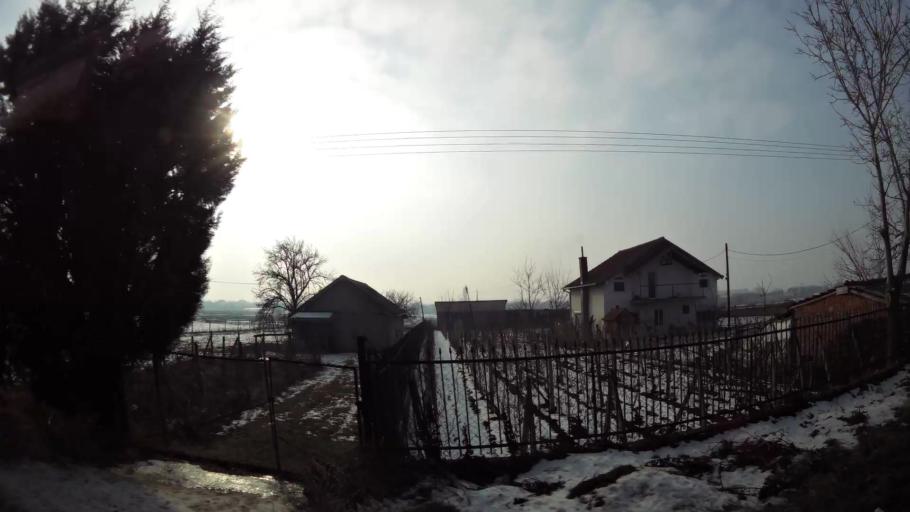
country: MK
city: Kadino
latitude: 41.9751
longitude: 21.6032
